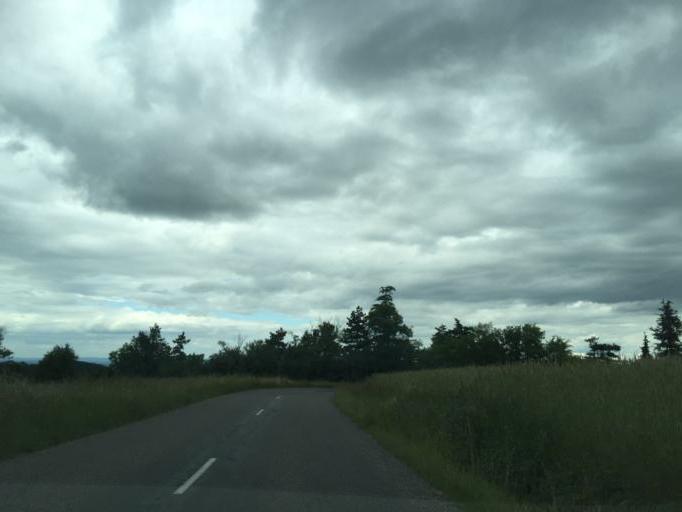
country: FR
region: Rhone-Alpes
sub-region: Departement de la Loire
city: Saint-Georges-Haute-Ville
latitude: 45.5144
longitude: 4.0980
